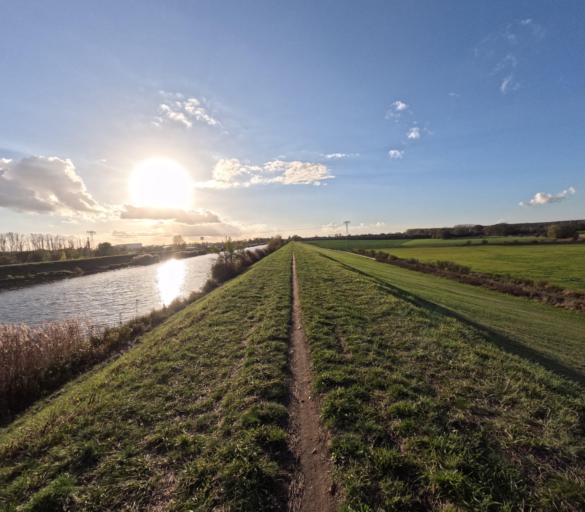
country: DE
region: Saxony-Anhalt
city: Gunthersdorf
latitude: 51.3572
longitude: 12.2003
